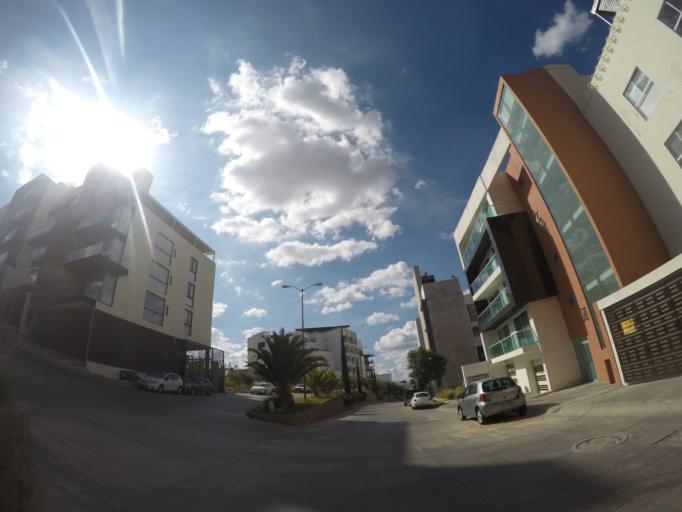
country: MX
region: San Luis Potosi
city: Escalerillas
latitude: 22.1233
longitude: -101.0343
